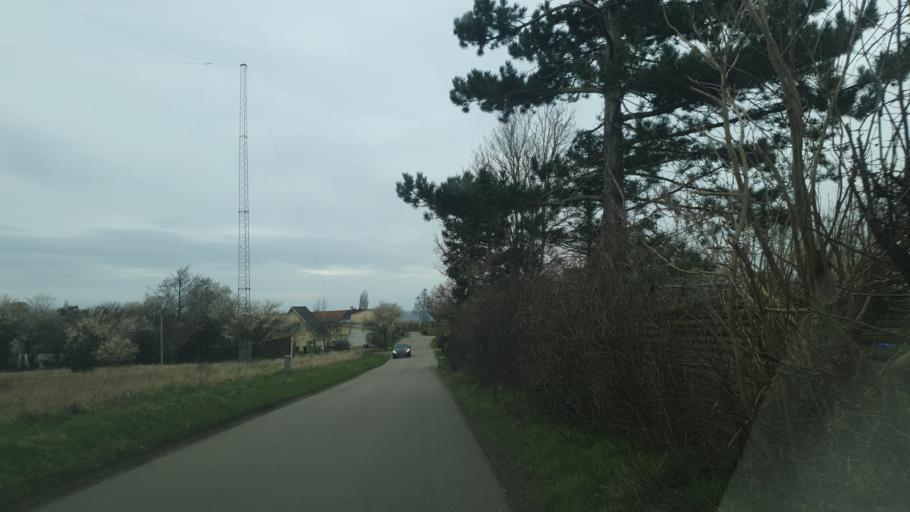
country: DK
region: Zealand
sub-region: Odsherred Kommune
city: Asnaes
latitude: 55.8328
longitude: 11.4238
